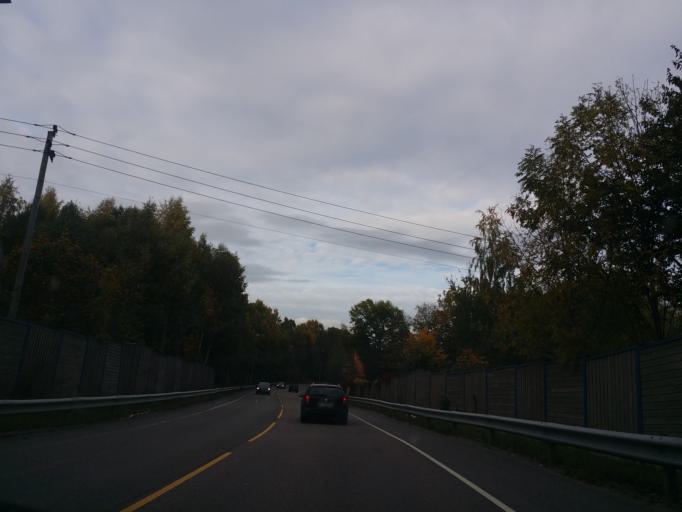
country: NO
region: Akershus
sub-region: Asker
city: Billingstad
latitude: 59.9102
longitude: 10.4890
